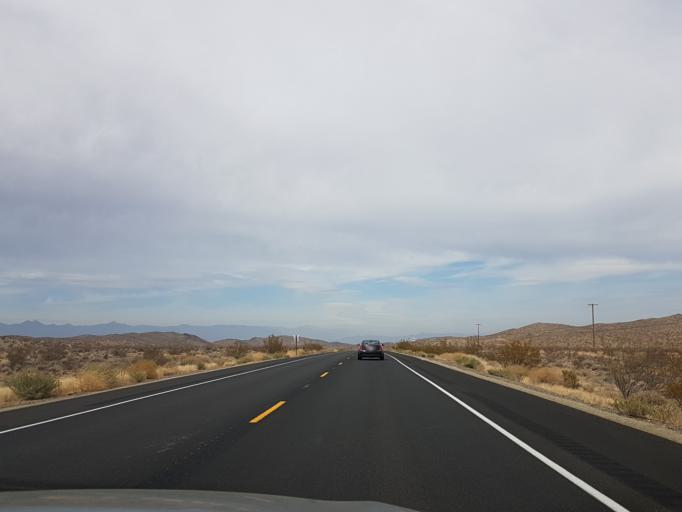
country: US
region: California
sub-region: Kern County
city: Ridgecrest
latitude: 35.5137
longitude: -117.6703
